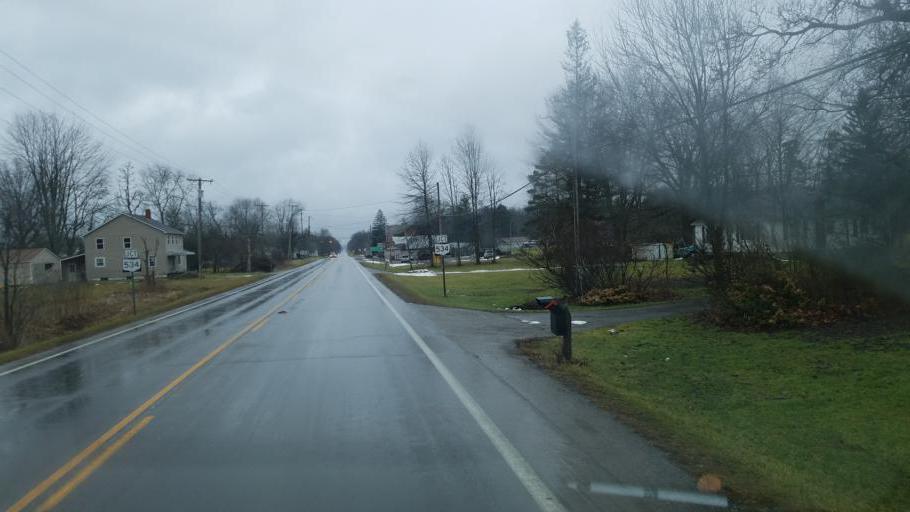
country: US
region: Ohio
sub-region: Geauga County
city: Middlefield
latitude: 41.3905
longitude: -80.9576
